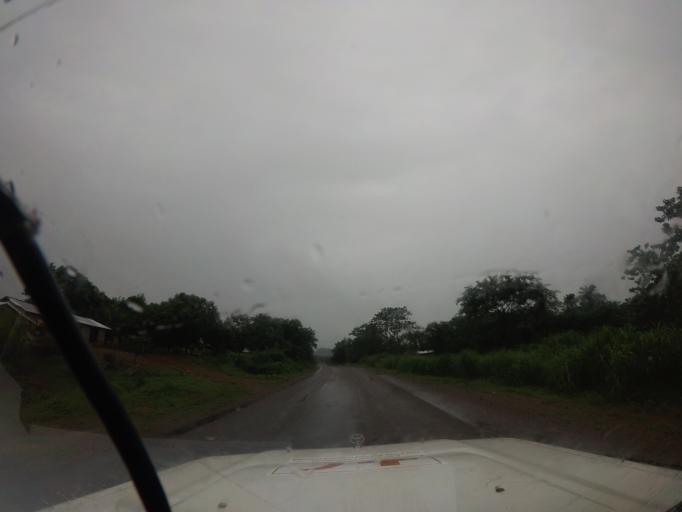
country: SL
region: Northern Province
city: Binkolo
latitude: 9.0686
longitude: -11.9536
